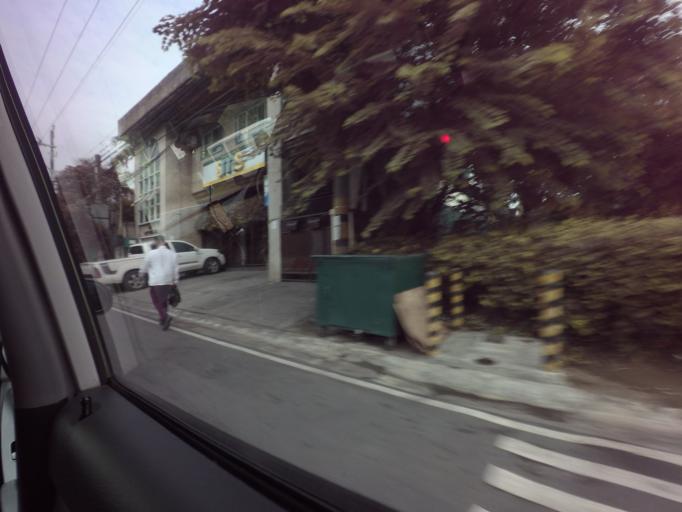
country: PH
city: Sambayanihan People's Village
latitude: 14.4486
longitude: 121.0263
